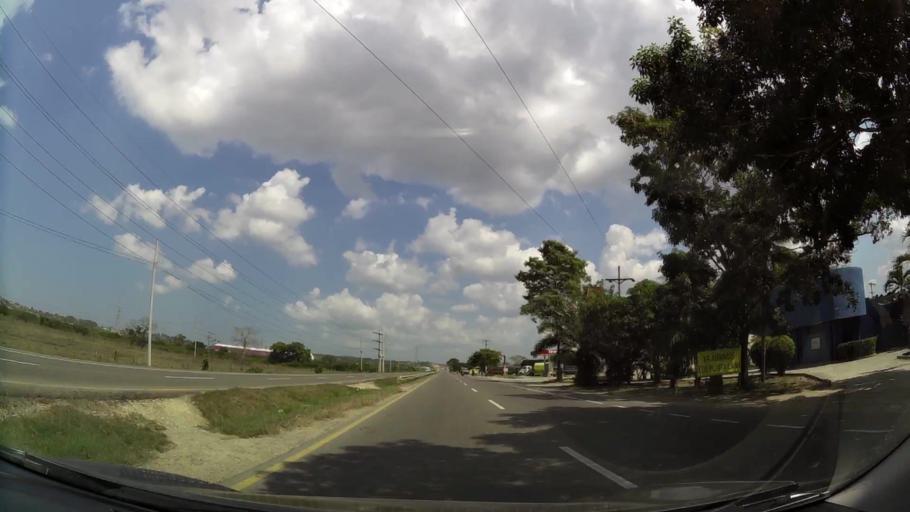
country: CO
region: Bolivar
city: Cartagena
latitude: 10.3529
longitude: -75.4785
